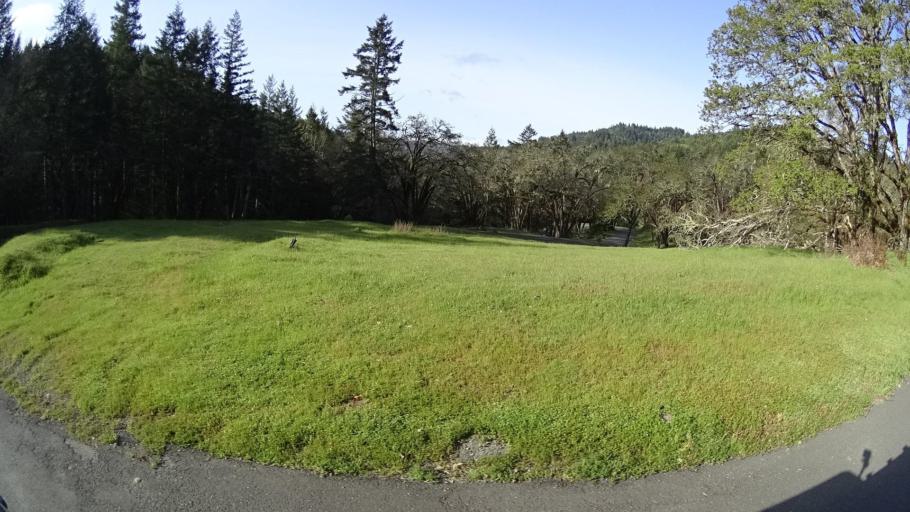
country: US
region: California
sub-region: Humboldt County
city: Blue Lake
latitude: 40.7091
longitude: -123.9365
